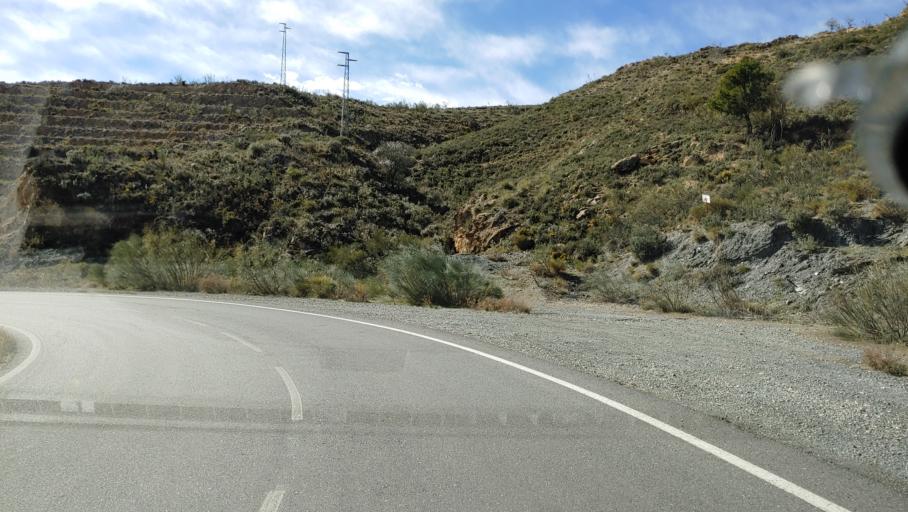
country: ES
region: Andalusia
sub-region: Provincia de Almeria
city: Ohanes
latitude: 37.0358
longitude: -2.7337
